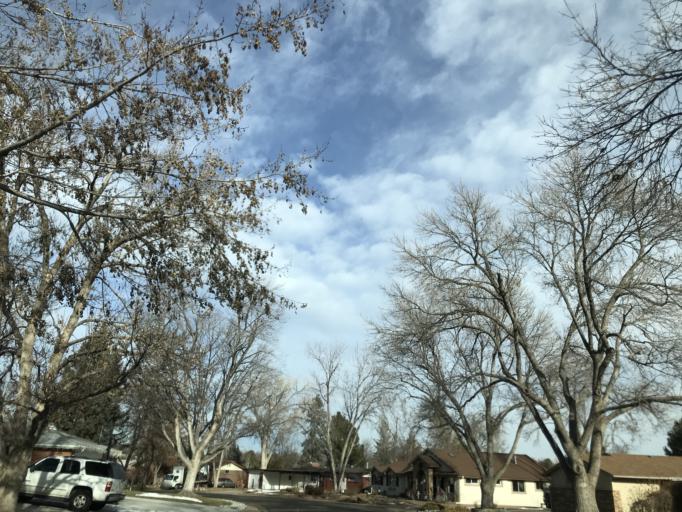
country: US
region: Colorado
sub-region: Arapahoe County
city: Columbine Valley
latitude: 39.5932
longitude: -105.0147
